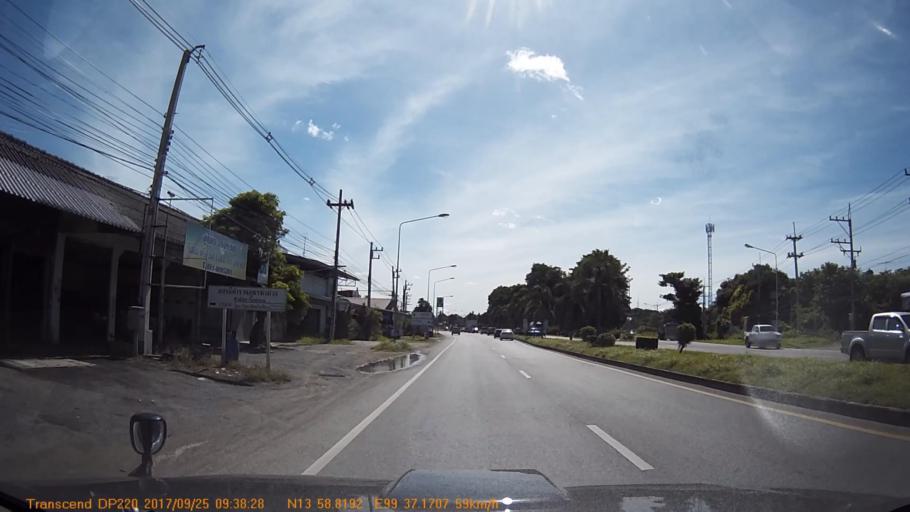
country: TH
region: Kanchanaburi
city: Tha Muang
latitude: 13.9803
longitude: 99.6195
